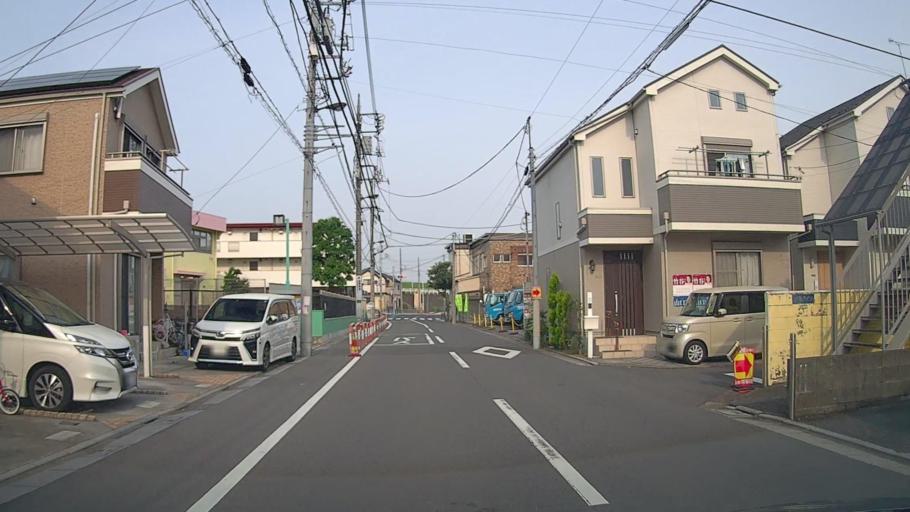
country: JP
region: Saitama
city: Kawaguchi
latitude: 35.7586
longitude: 139.7609
